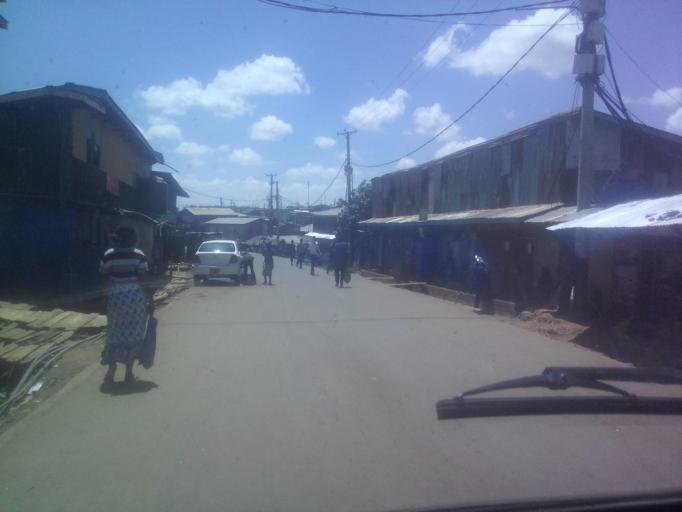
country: KE
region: Nairobi Area
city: Nairobi
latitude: -1.3147
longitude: 36.7964
